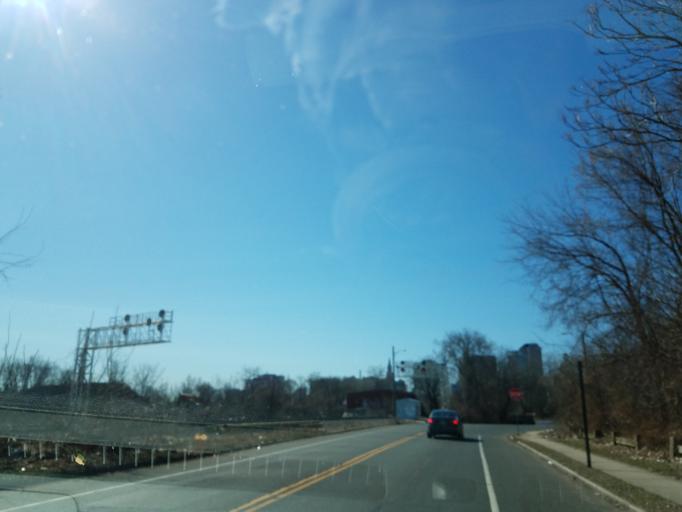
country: US
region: Connecticut
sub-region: Hartford County
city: Hartford
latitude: 41.7789
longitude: -72.6725
